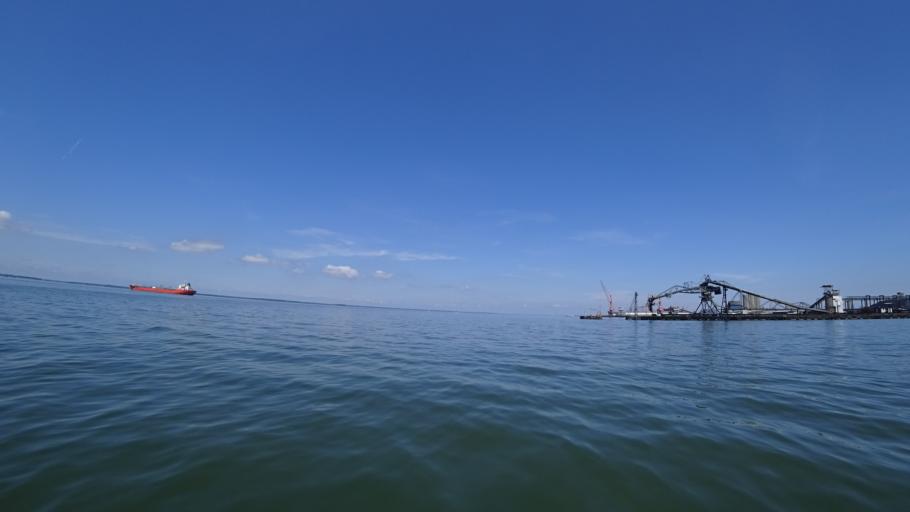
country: US
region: Virginia
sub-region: City of Newport News
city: Newport News
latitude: 36.9606
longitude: -76.4217
